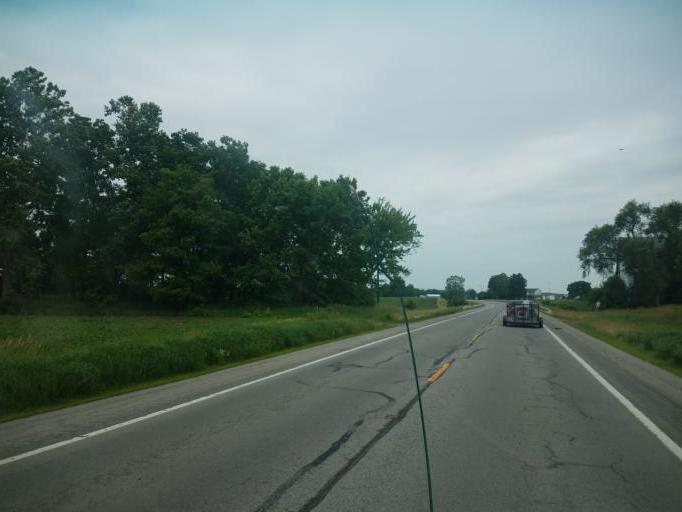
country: US
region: Ohio
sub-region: Hardin County
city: Ada
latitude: 40.7161
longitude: -83.7624
